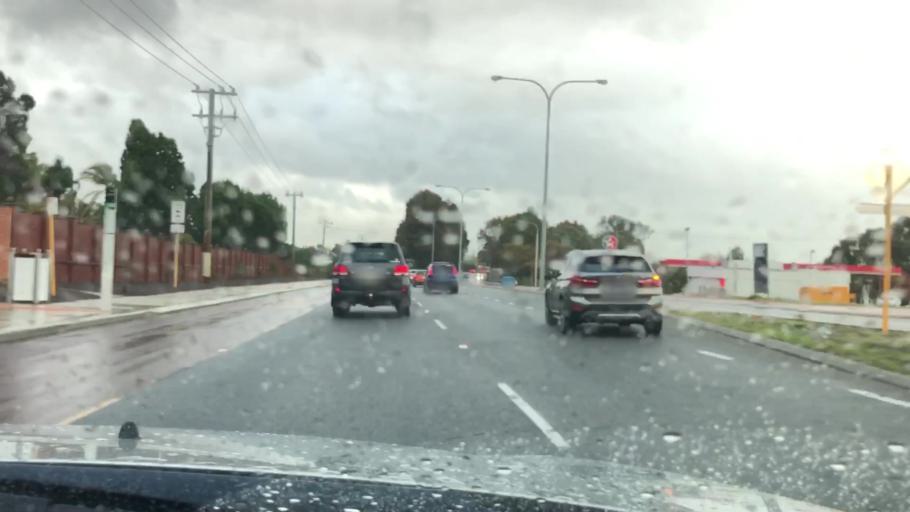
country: AU
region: Western Australia
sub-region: Canning
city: Canning Vale
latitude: -32.0809
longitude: 115.9074
